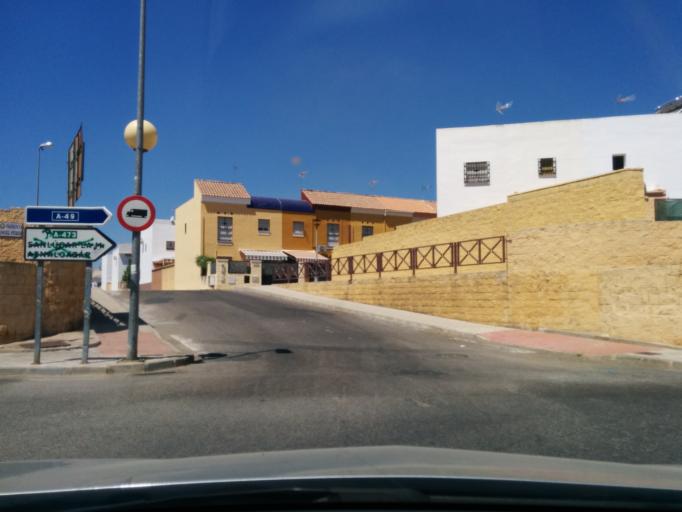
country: ES
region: Andalusia
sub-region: Provincia de Sevilla
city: Benacazon
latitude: 37.3551
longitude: -6.1951
